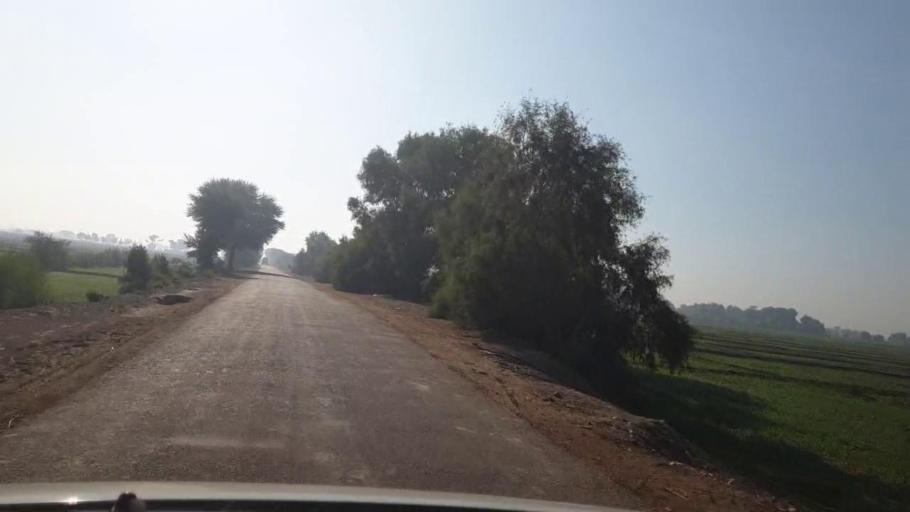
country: PK
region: Sindh
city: Dadu
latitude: 26.6608
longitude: 67.8197
